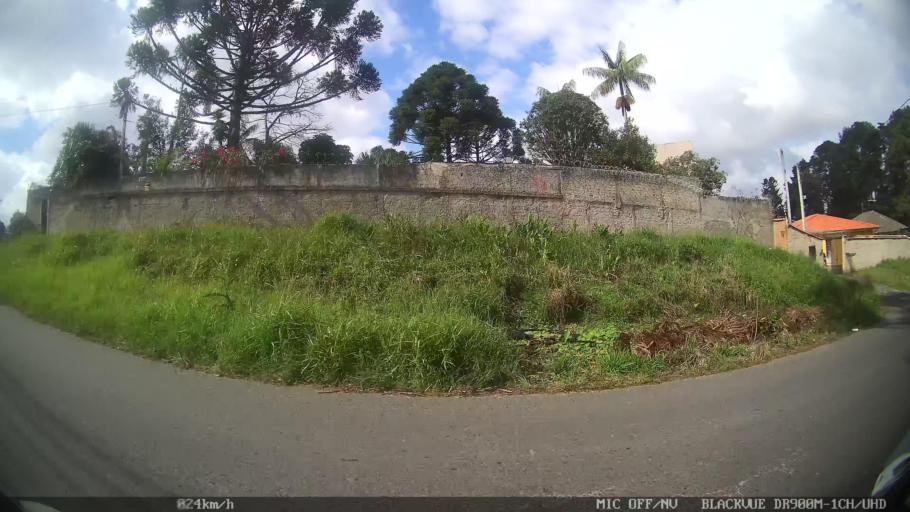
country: BR
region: Parana
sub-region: Colombo
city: Colombo
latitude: -25.3574
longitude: -49.2105
